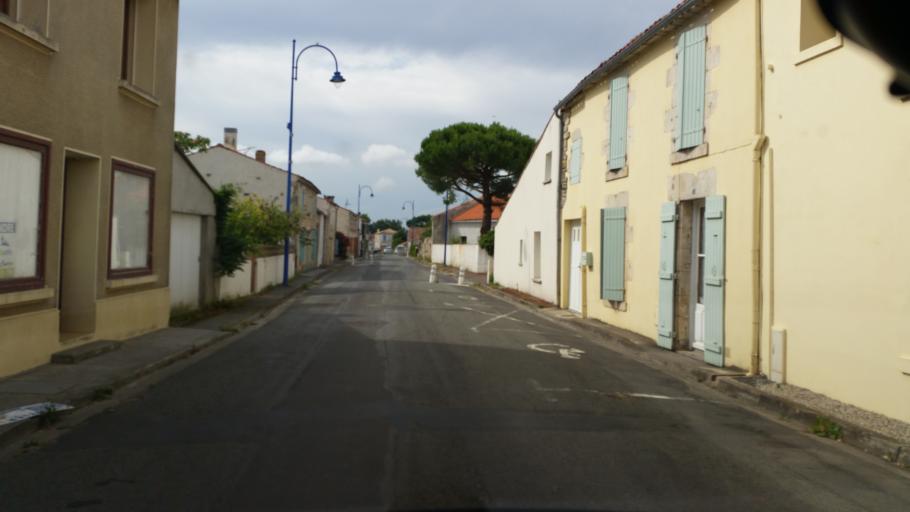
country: FR
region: Poitou-Charentes
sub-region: Departement de la Charente-Maritime
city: Courcon
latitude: 46.1858
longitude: -0.8606
